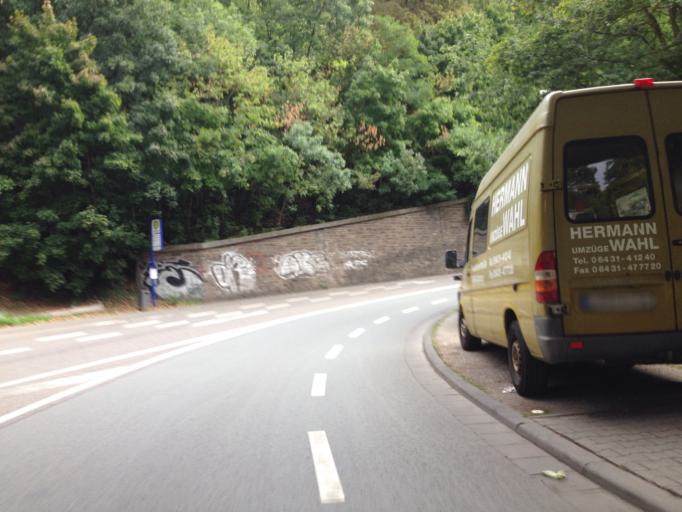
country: DE
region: Hesse
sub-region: Regierungsbezirk Giessen
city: Limburg an der Lahn
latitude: 50.3865
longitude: 8.0682
